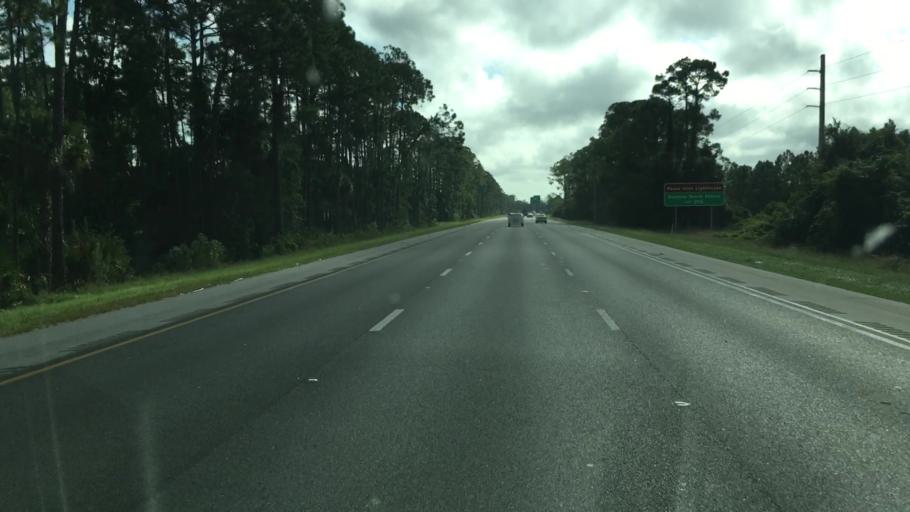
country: US
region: Florida
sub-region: Volusia County
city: Port Orange
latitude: 29.1186
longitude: -81.0420
